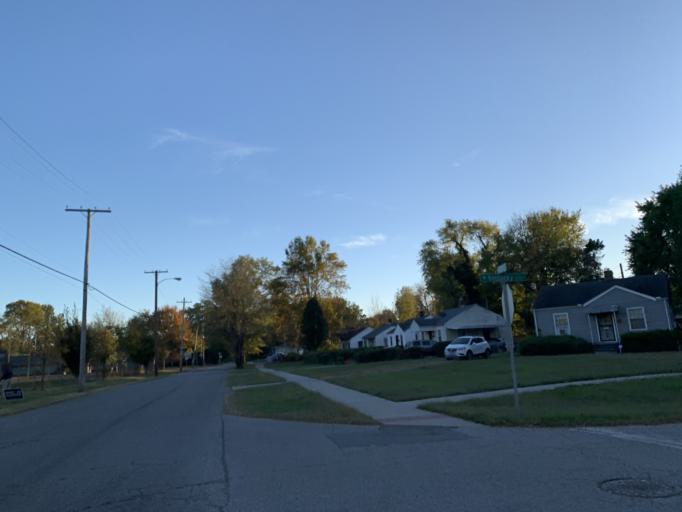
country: US
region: Indiana
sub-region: Floyd County
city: New Albany
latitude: 38.2462
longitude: -85.8275
